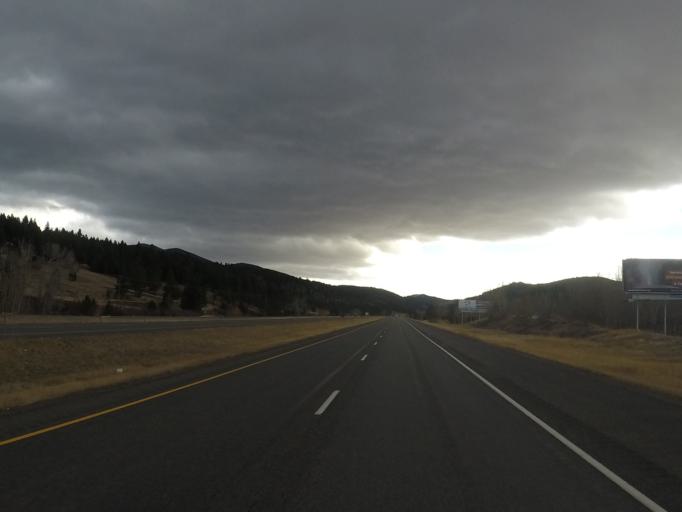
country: US
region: Montana
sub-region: Jefferson County
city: Clancy
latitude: 46.4027
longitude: -112.0168
